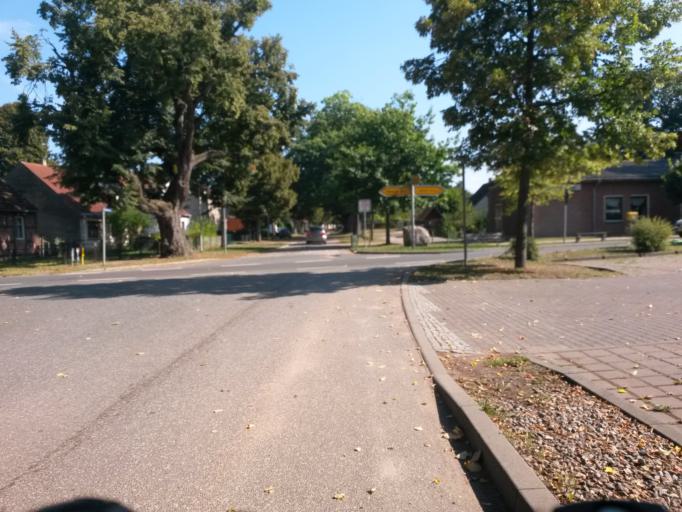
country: DE
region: Brandenburg
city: Templin
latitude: 53.0507
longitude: 13.5302
